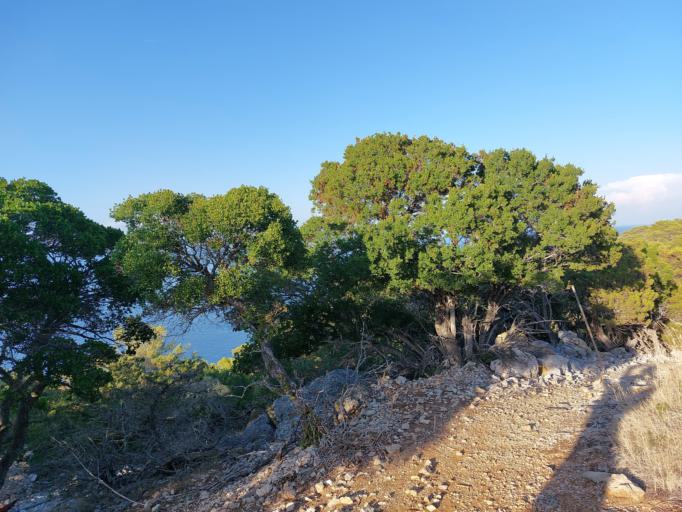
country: HR
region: Dubrovacko-Neretvanska
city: Smokvica
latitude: 42.7746
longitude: 16.7863
